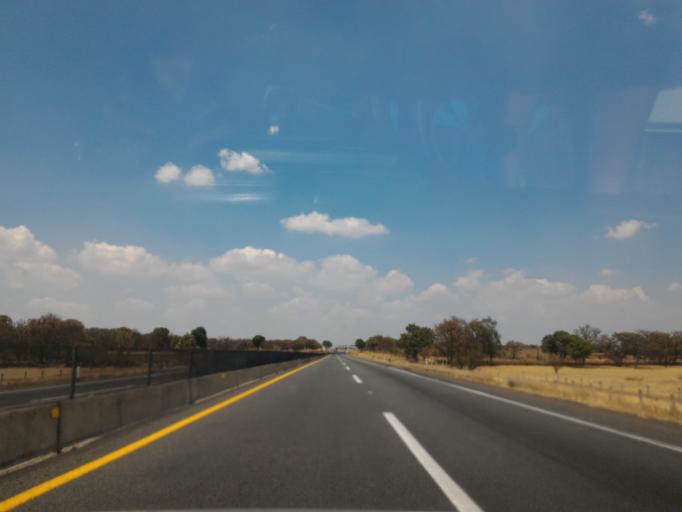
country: MX
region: Jalisco
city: Tepatitlan de Morelos
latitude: 20.8635
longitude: -102.7609
